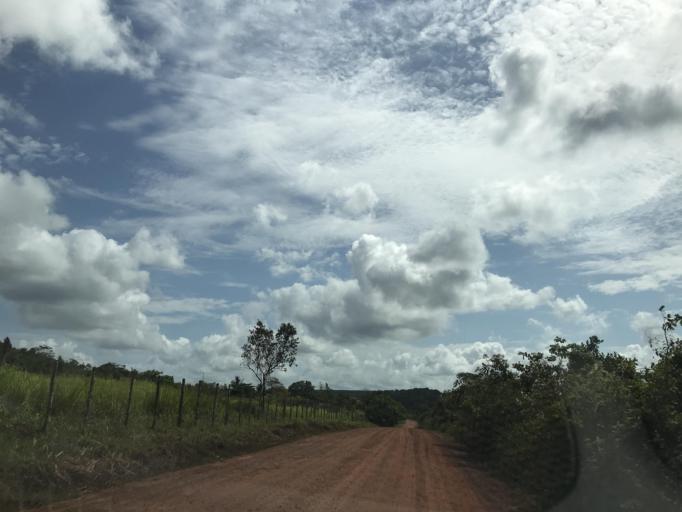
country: BR
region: Bahia
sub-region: Entre Rios
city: Entre Rios
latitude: -12.1670
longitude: -38.0866
